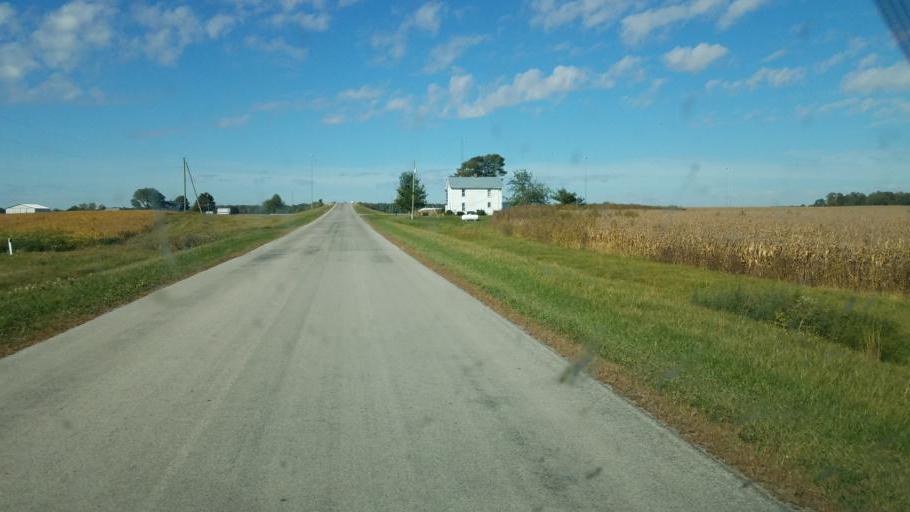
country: US
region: Ohio
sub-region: Wyandot County
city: Upper Sandusky
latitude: 40.8038
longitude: -83.2310
